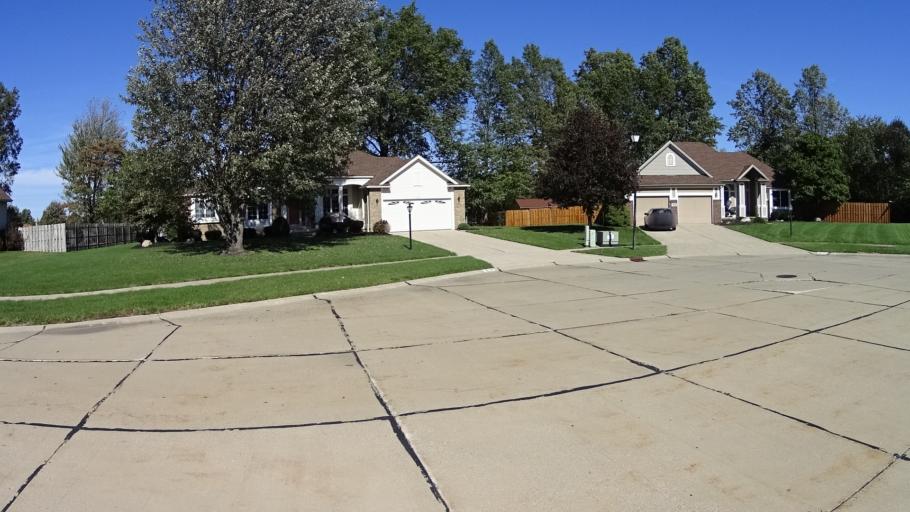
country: US
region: Ohio
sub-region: Lorain County
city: Amherst
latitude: 41.3889
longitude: -82.2220
